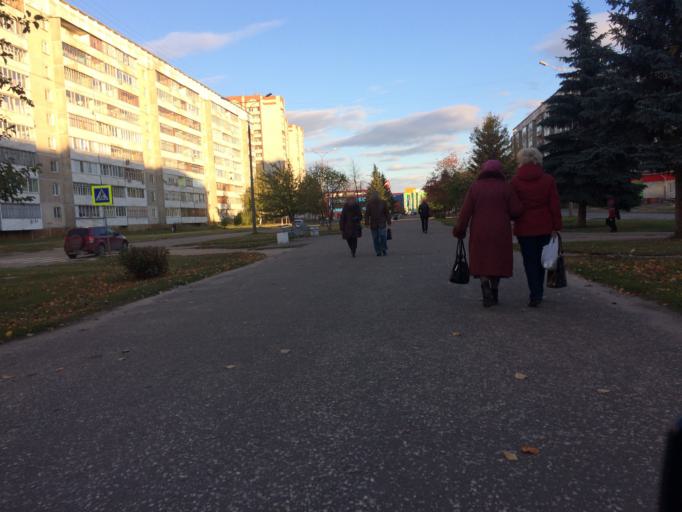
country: RU
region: Mariy-El
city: Yoshkar-Ola
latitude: 56.6297
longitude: 47.9222
